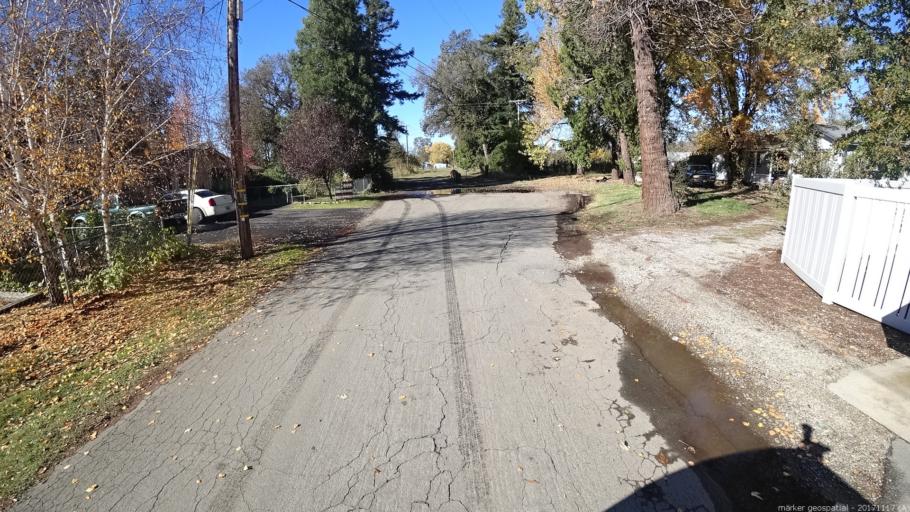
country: US
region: California
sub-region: Shasta County
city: Anderson
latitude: 40.4513
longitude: -122.2435
